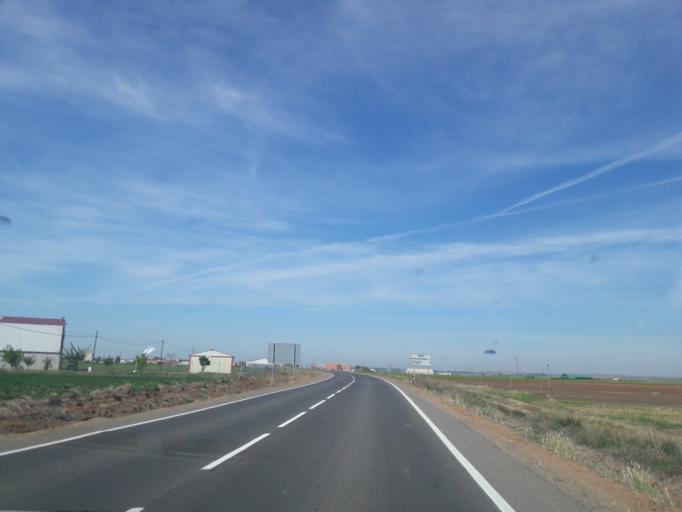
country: ES
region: Castille and Leon
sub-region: Provincia de Salamanca
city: Babilafuente
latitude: 40.9825
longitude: -5.4119
